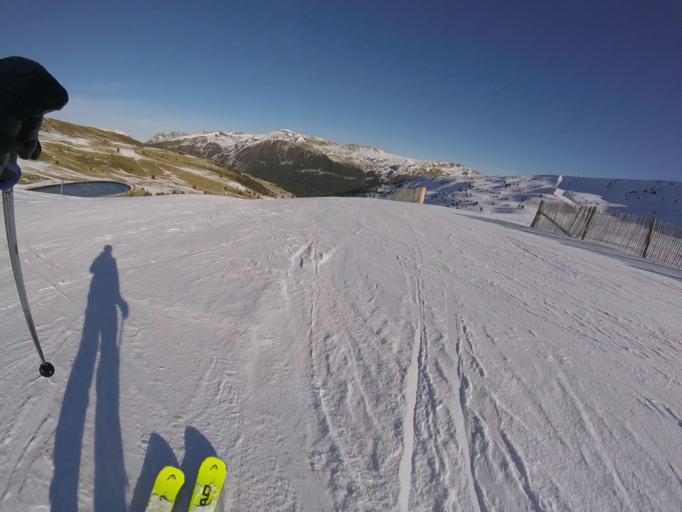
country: AD
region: Canillo
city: El Tarter
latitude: 42.5501
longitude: 1.6585
